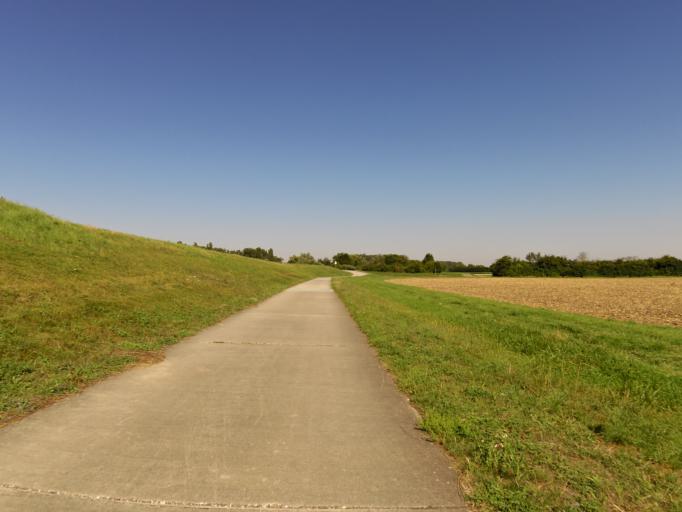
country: DE
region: Rheinland-Pfalz
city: Oppenheim
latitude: 49.8379
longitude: 8.4103
